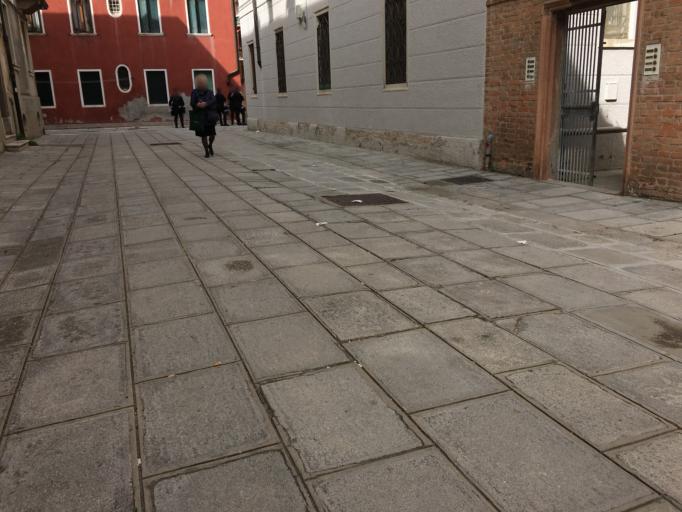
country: IT
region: Veneto
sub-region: Provincia di Venezia
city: Lido
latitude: 45.4284
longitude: 12.3618
